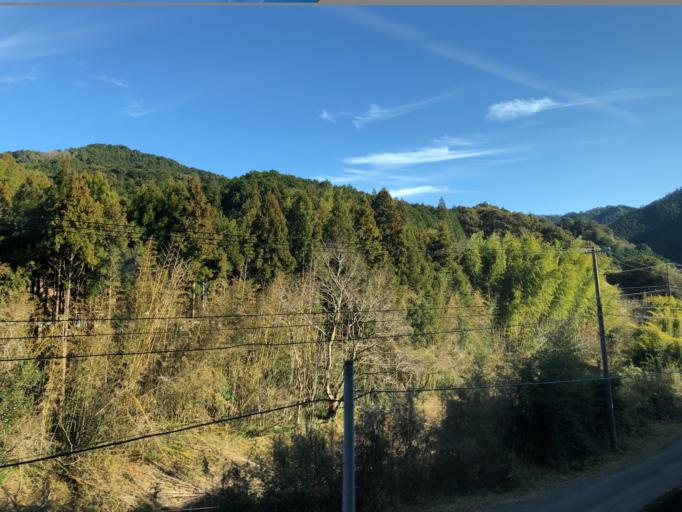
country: JP
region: Kochi
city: Nakamura
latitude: 33.1237
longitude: 133.1192
